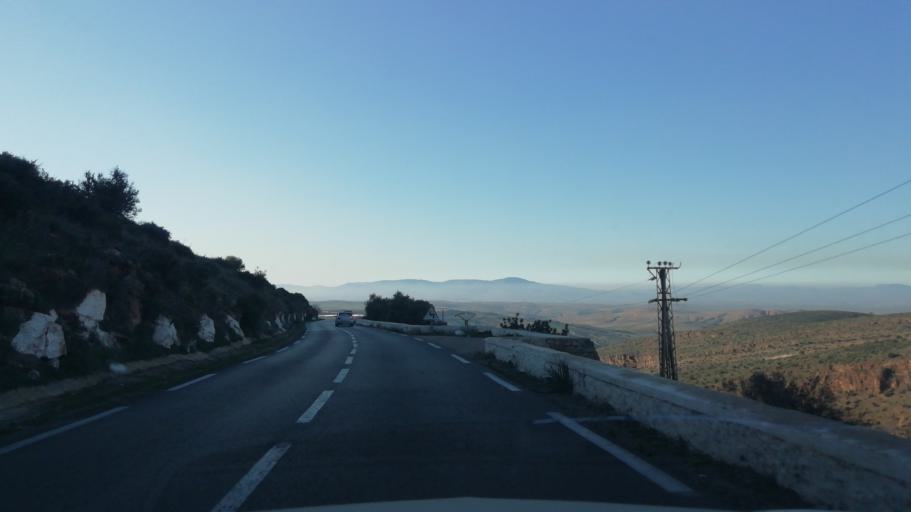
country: DZ
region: Tlemcen
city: Beni Mester
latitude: 34.8508
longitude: -1.4547
